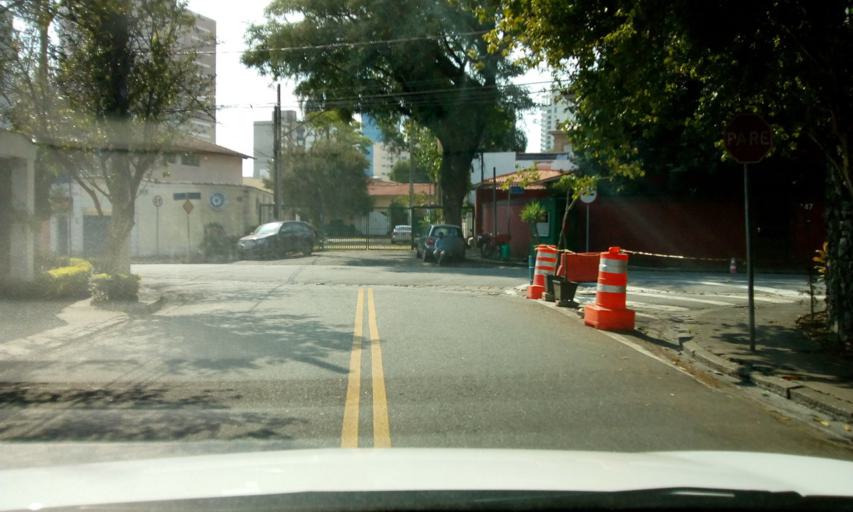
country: BR
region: Sao Paulo
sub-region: Sao Paulo
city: Sao Paulo
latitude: -23.6064
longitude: -46.6776
